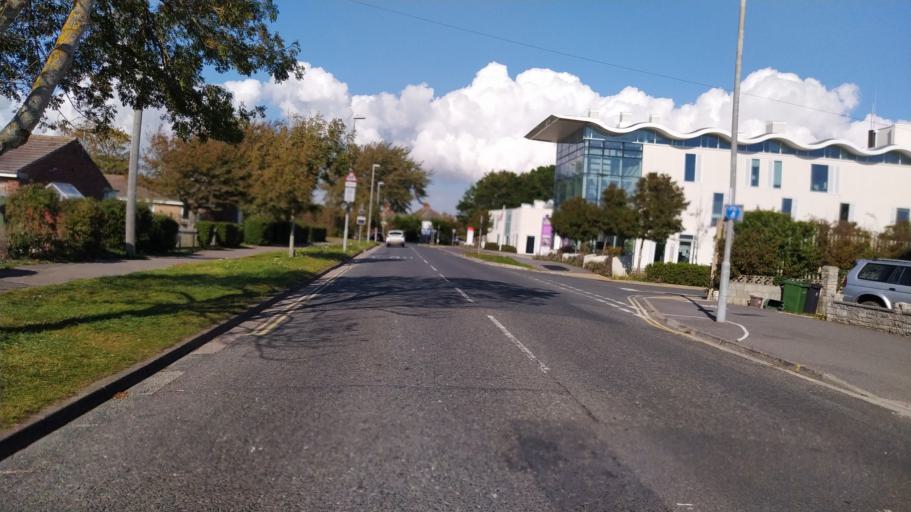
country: GB
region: England
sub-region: Dorset
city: Weymouth
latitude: 50.6111
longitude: -2.4813
